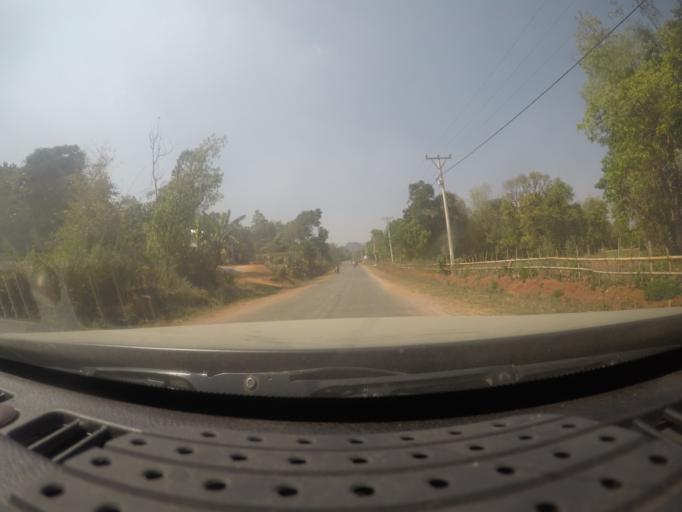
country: MM
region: Mandalay
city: Kyaukse
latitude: 21.1214
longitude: 96.4606
